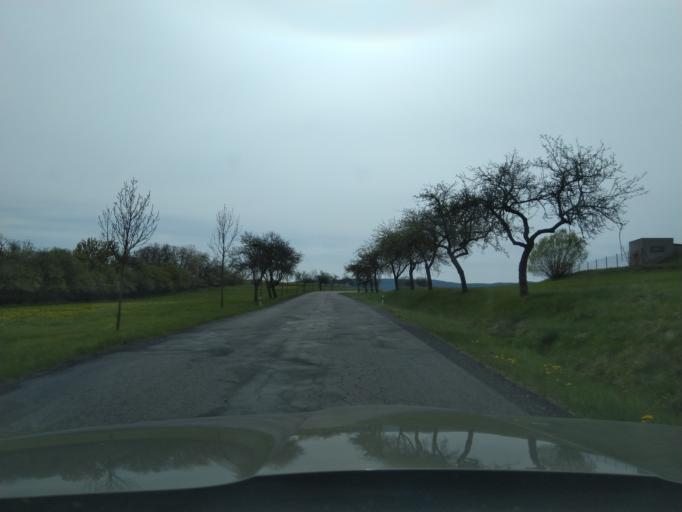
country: CZ
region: Plzensky
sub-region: Okres Klatovy
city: Kasperske Hory
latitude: 49.2037
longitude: 13.6118
